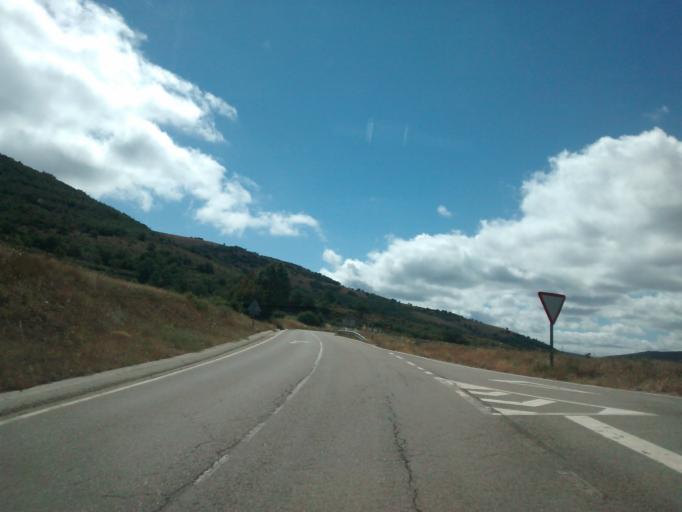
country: ES
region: Cantabria
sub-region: Provincia de Cantabria
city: Mataporquera
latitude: 42.8915
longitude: -4.0774
